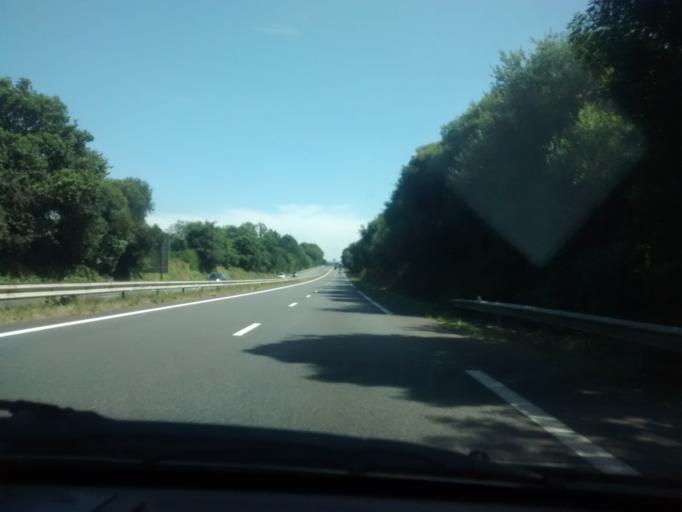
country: FR
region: Brittany
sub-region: Departement des Cotes-d'Armor
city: Graces
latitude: 48.5567
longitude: -3.1783
